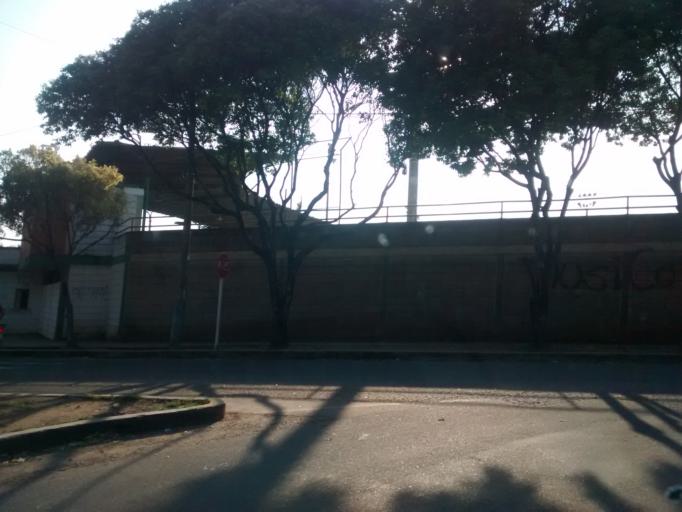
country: CO
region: Santander
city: Bucaramanga
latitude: 7.0979
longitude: -73.1269
